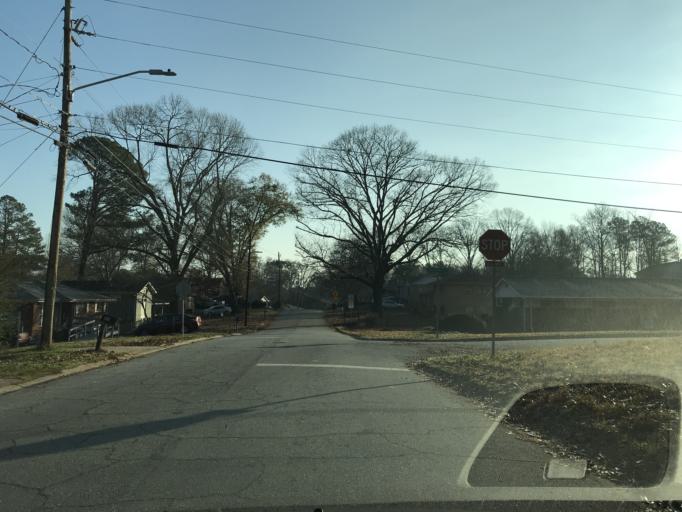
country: US
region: Georgia
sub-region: Fulton County
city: College Park
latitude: 33.6145
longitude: -84.4338
